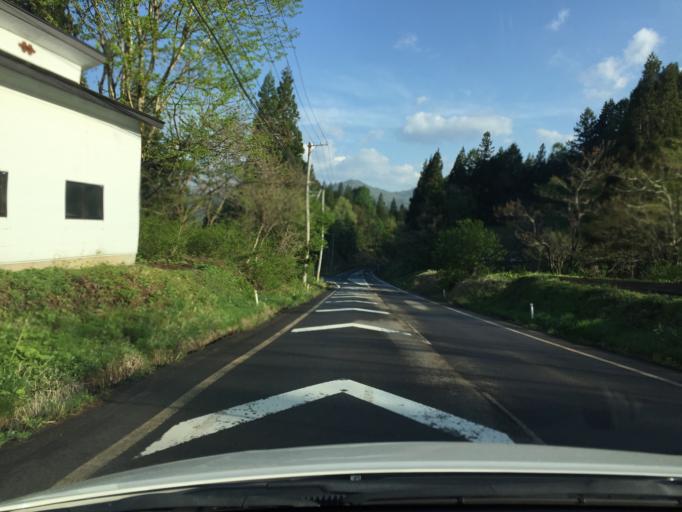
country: JP
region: Fukushima
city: Kitakata
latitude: 37.6616
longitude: 139.9907
